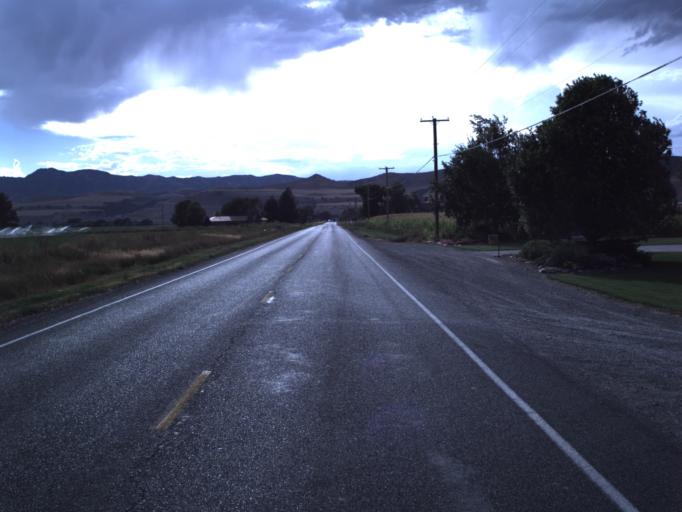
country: US
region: Utah
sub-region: Cache County
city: Lewiston
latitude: 41.9755
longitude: -111.9108
